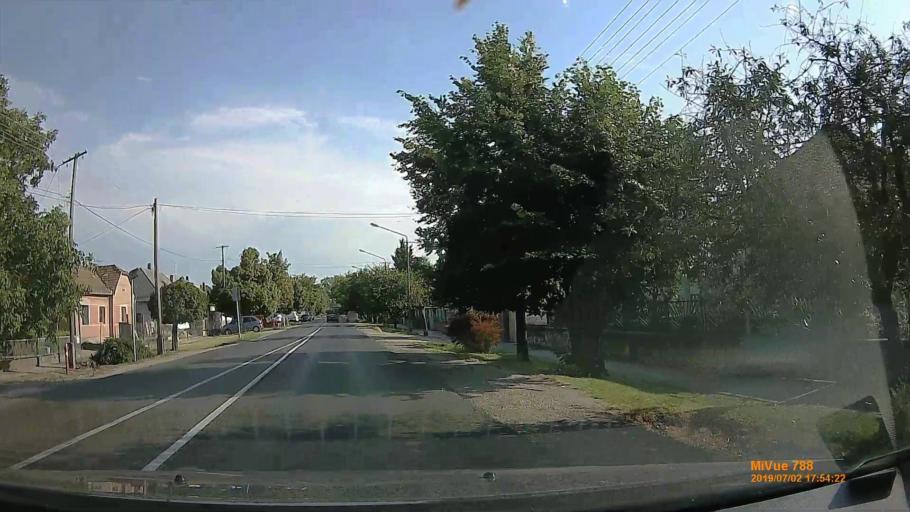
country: HU
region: Gyor-Moson-Sopron
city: Mosonmagyarovar
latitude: 47.8552
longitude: 17.2654
